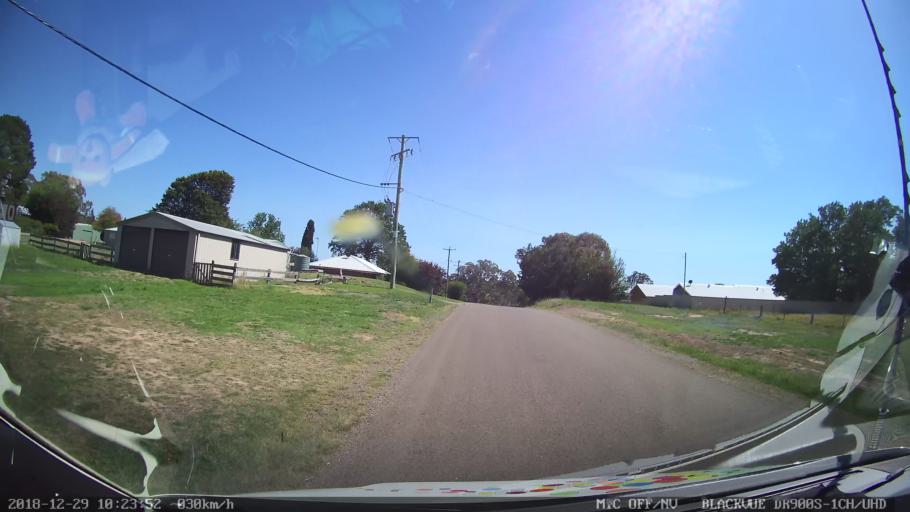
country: AU
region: New South Wales
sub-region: Yass Valley
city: Gundaroo
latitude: -34.9132
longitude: 149.4370
